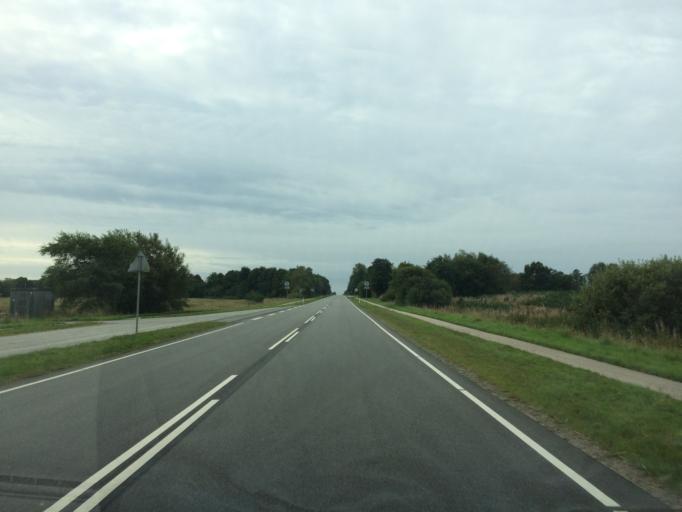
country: DK
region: Central Jutland
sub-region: Herning Kommune
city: Lind
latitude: 56.0818
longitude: 8.9828
